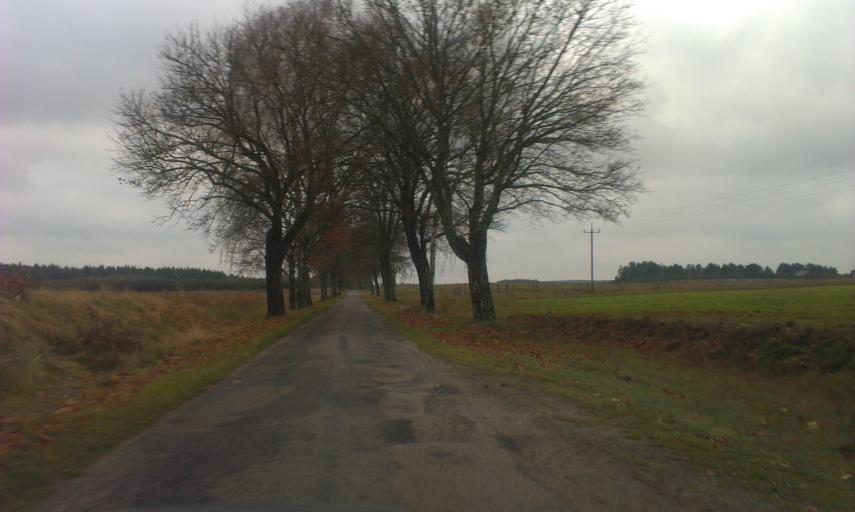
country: PL
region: West Pomeranian Voivodeship
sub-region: Powiat szczecinecki
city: Szczecinek
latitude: 53.7961
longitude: 16.6780
